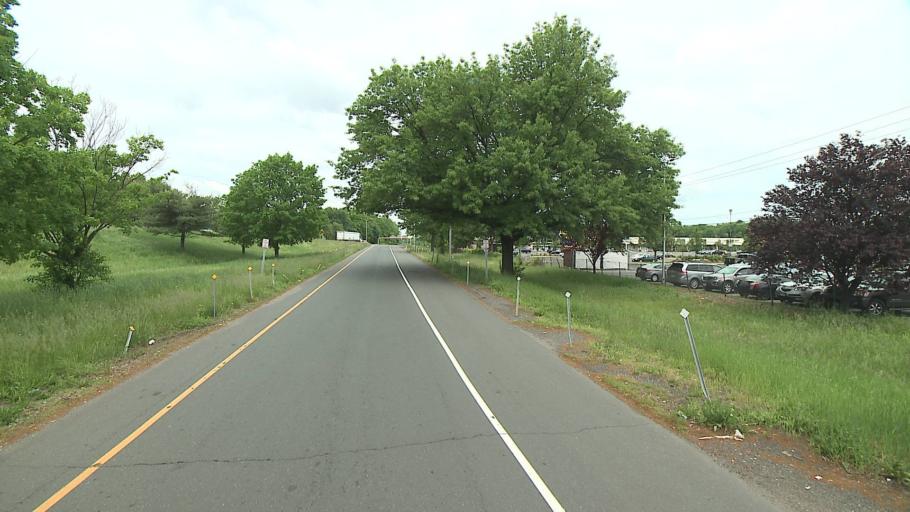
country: US
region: Connecticut
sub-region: Hartford County
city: Thompsonville
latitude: 41.9981
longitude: -72.5849
